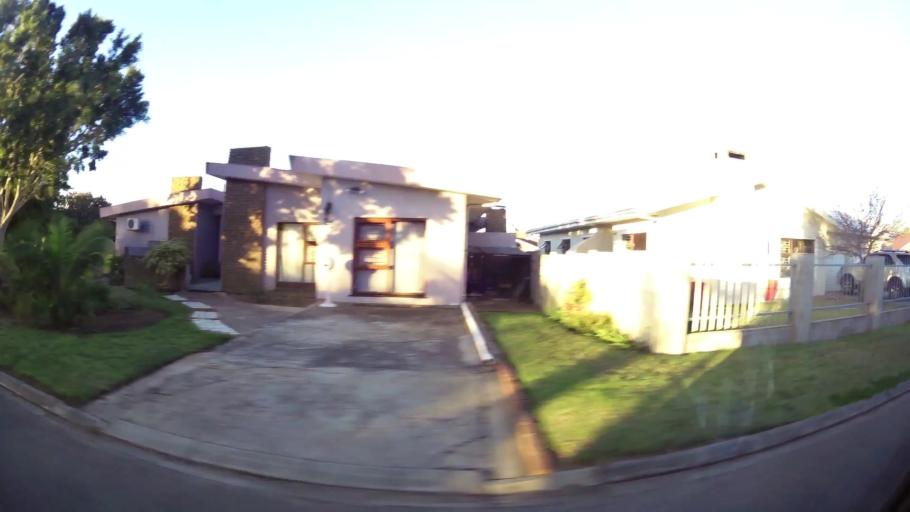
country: ZA
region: Western Cape
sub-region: Eden District Municipality
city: Riversdale
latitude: -34.0843
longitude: 21.2468
